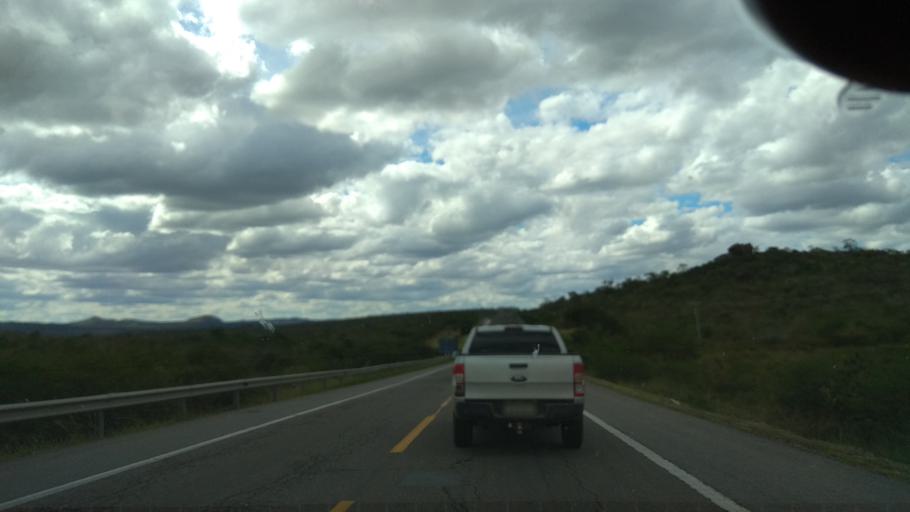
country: BR
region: Bahia
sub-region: Santa Ines
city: Santa Ines
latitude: -13.0028
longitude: -39.9555
